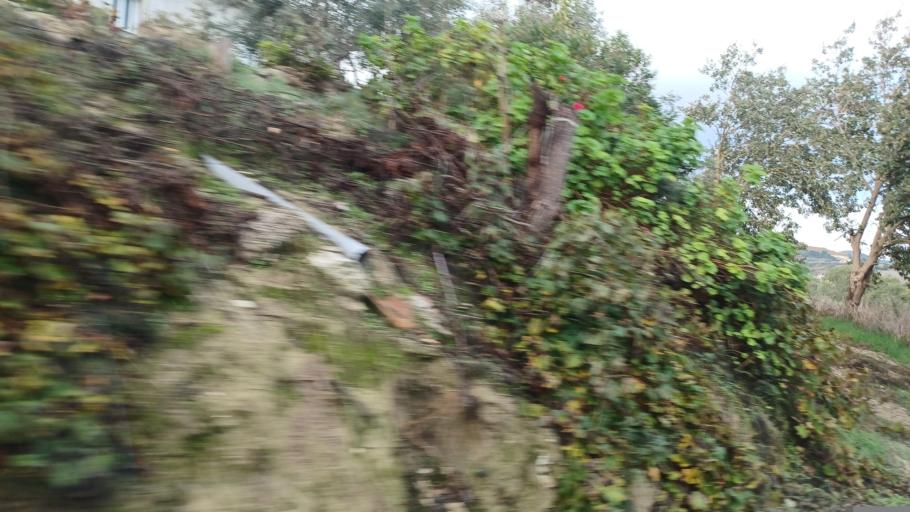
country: CY
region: Pafos
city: Tala
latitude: 34.8931
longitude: 32.4772
